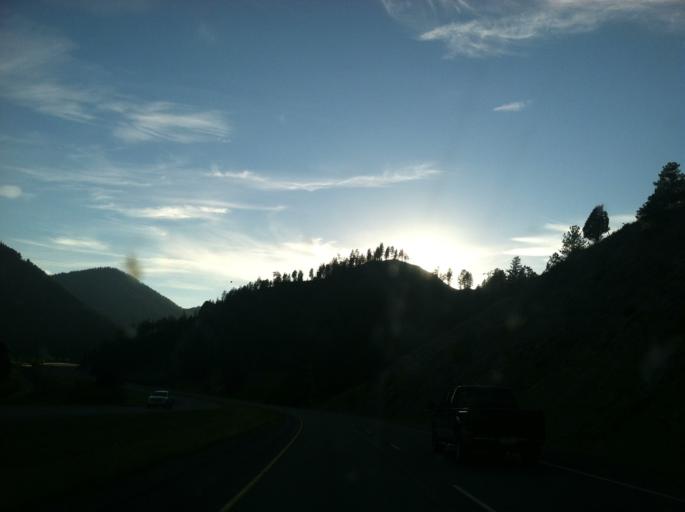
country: US
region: Montana
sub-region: Missoula County
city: Clinton
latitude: 46.7037
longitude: -113.4702
